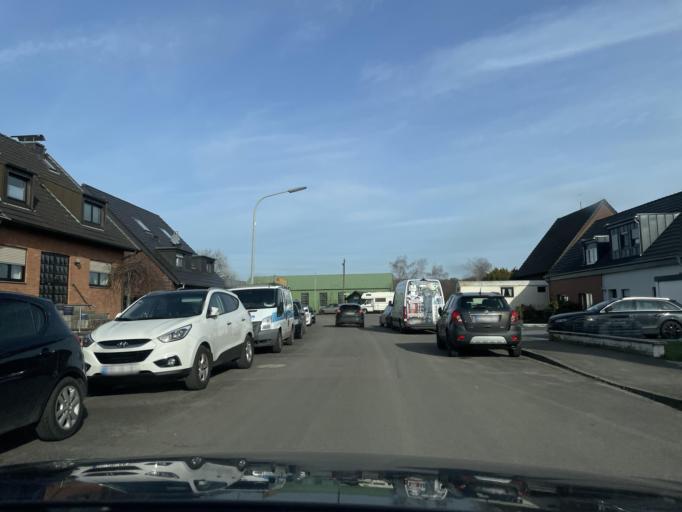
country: DE
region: North Rhine-Westphalia
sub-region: Regierungsbezirk Dusseldorf
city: Monchengladbach
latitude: 51.2298
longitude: 6.4528
